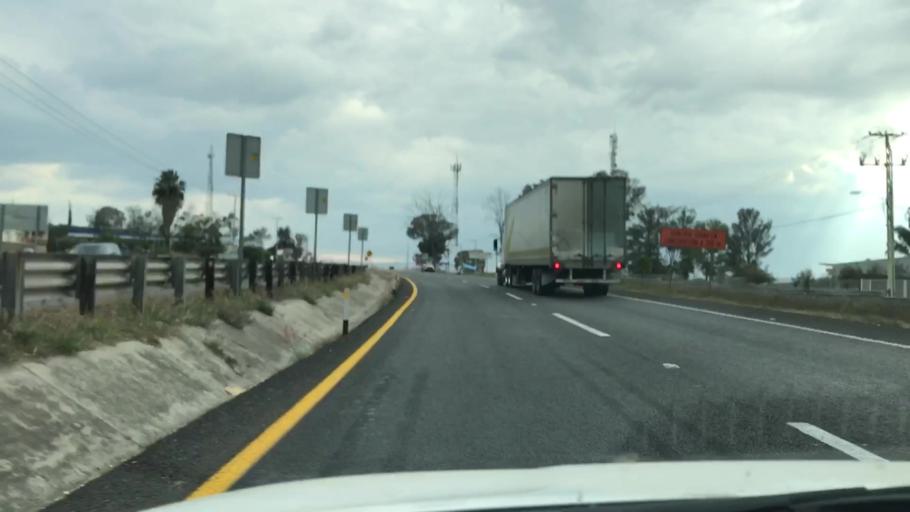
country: MX
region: Guanajuato
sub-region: Irapuato
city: San Ignacio de Rivera (Ojo de Agua)
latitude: 20.5669
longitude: -101.4468
